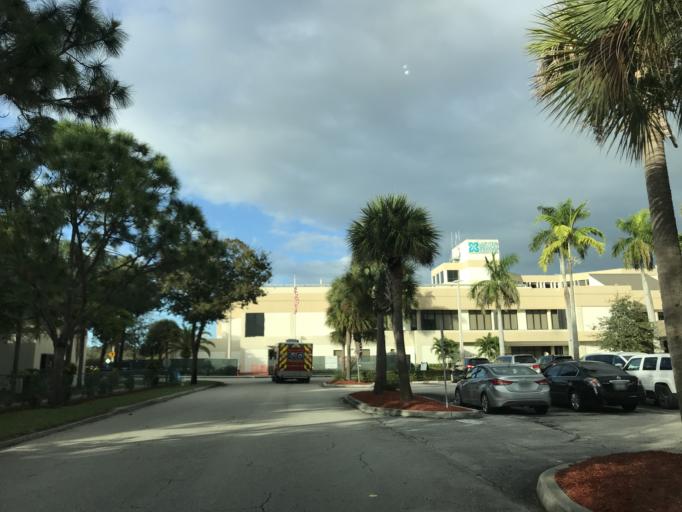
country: US
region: Florida
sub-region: Palm Beach County
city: Jupiter
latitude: 26.9216
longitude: -80.0969
